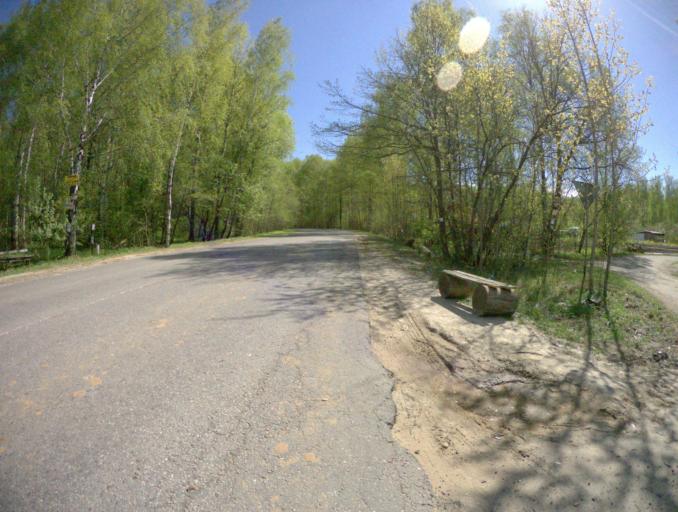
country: RU
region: Vladimir
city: Orgtrud
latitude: 56.1988
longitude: 40.5895
